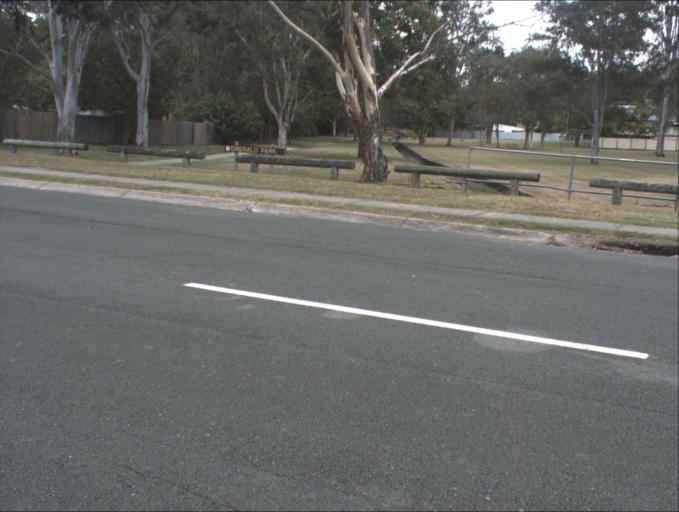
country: AU
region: Queensland
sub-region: Logan
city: Beenleigh
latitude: -27.7181
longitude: 153.1893
